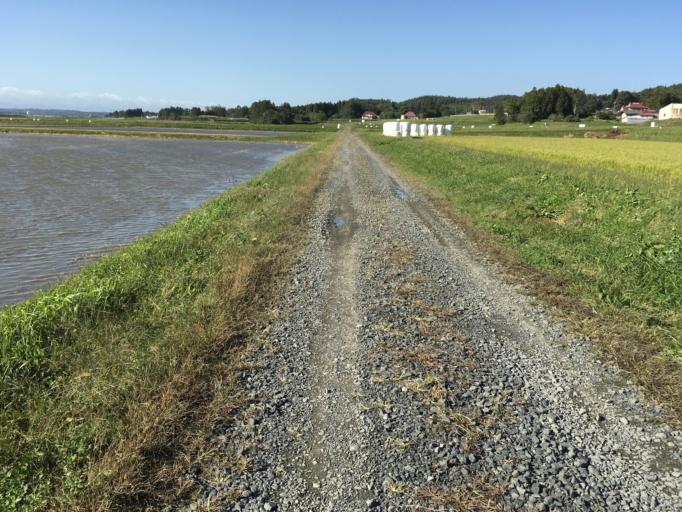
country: JP
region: Iwate
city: Ichinoseki
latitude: 38.8138
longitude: 141.2134
